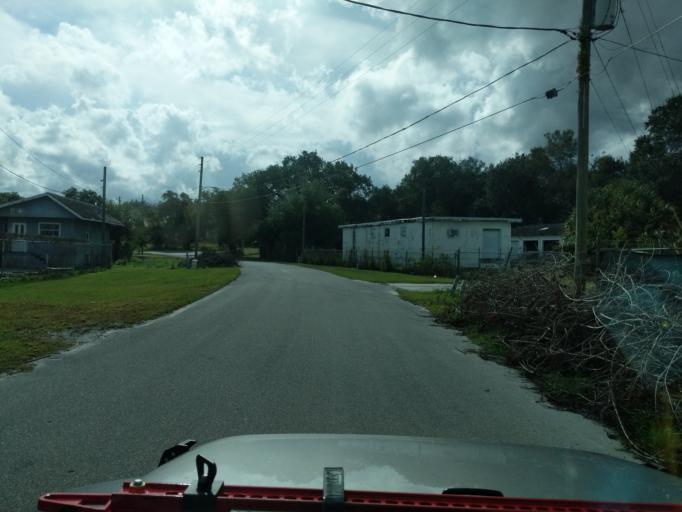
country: US
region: Florida
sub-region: Lake County
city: Clermont
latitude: 28.5575
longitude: -81.7734
